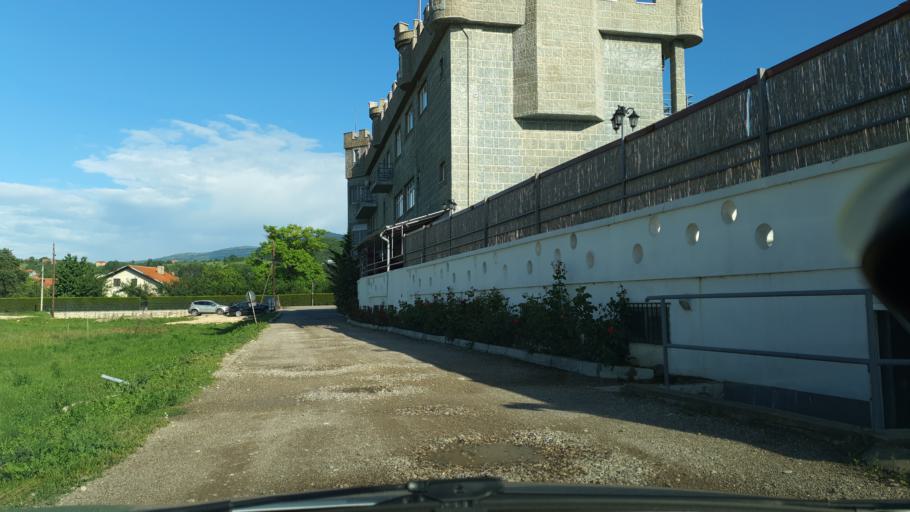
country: RS
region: Central Serbia
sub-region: Zajecarski Okrug
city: Soko Banja
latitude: 43.6472
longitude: 21.8747
